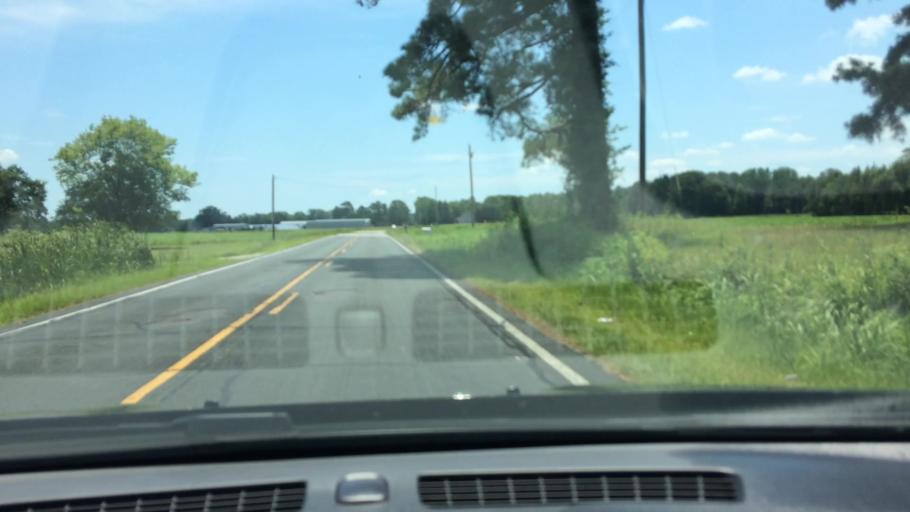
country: US
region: North Carolina
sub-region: Beaufort County
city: Washington
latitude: 35.5958
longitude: -77.1479
